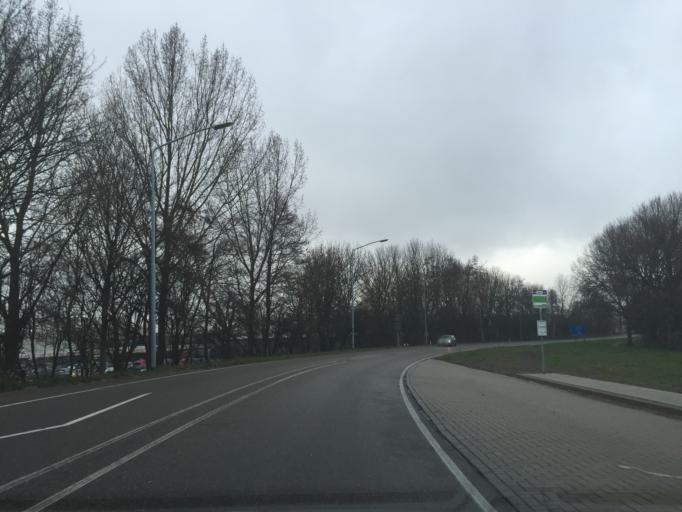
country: NL
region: South Holland
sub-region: Gemeente Kaag en Braassem
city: Oude Wetering
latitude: 52.2207
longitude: 4.6414
